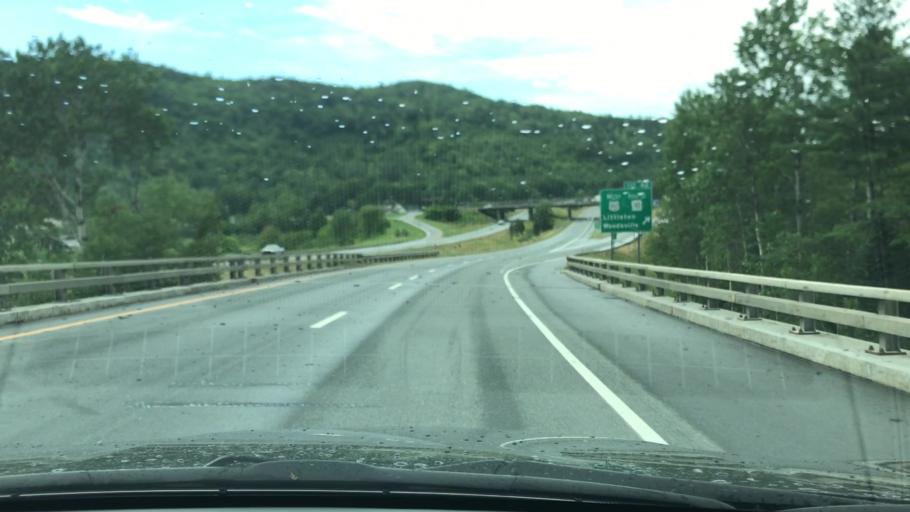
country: US
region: New Hampshire
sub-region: Grafton County
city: Littleton
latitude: 44.3047
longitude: -71.7963
